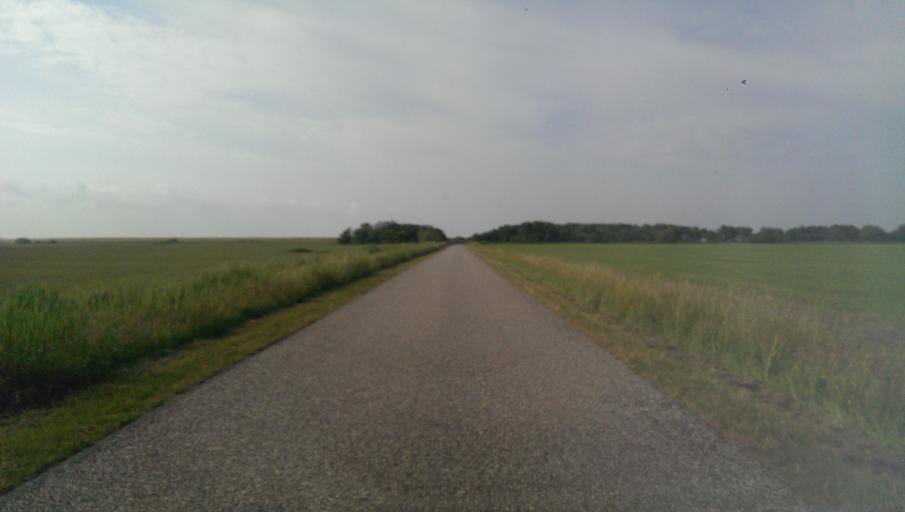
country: DK
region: South Denmark
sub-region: Esbjerg Kommune
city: Tjaereborg
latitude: 55.4376
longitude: 8.6120
